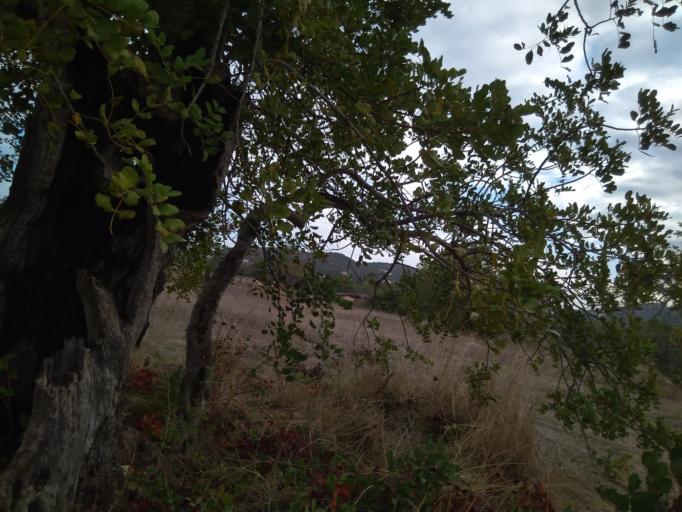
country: PT
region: Faro
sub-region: Faro
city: Santa Barbara de Nexe
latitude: 37.1043
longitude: -7.9569
